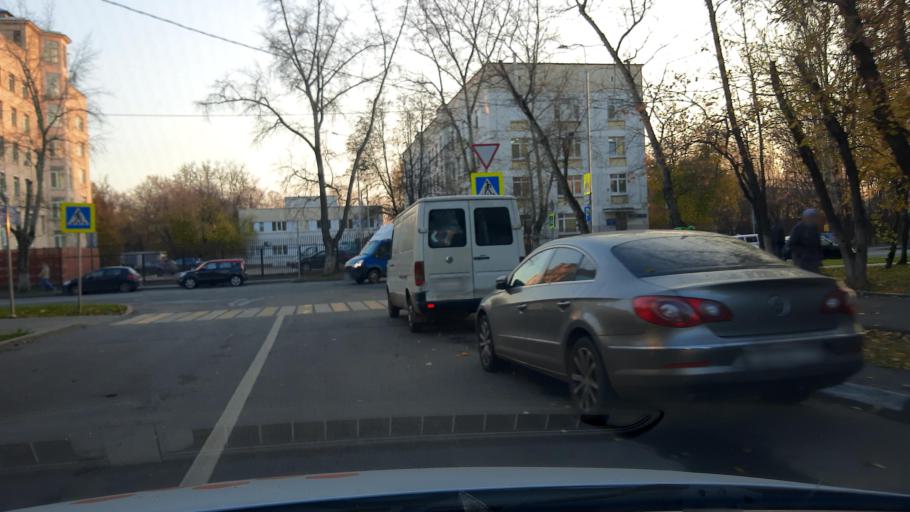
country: RU
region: Moscow
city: Novyye Kuz'minki
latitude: 55.6941
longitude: 37.7484
